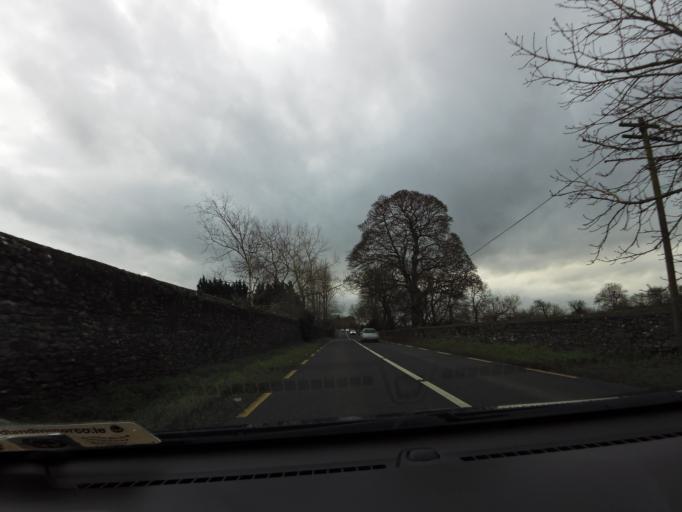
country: IE
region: Leinster
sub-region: Kilkenny
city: Kilkenny
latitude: 52.7002
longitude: -7.2670
